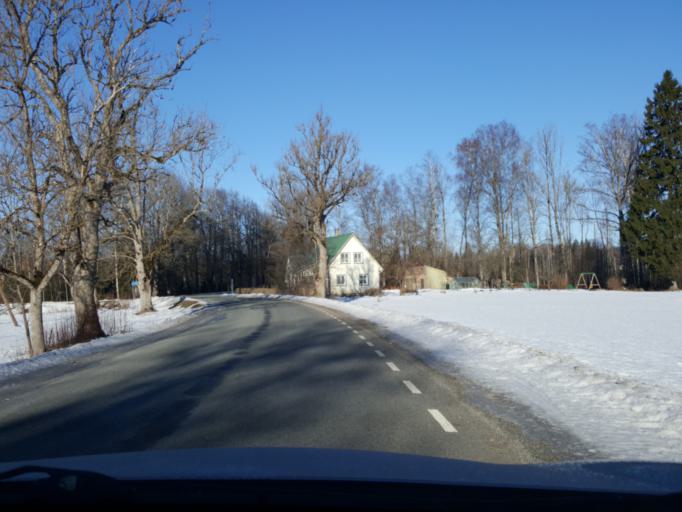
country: EE
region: Viljandimaa
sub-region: Viljandi linn
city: Viljandi
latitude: 58.4188
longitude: 25.5420
